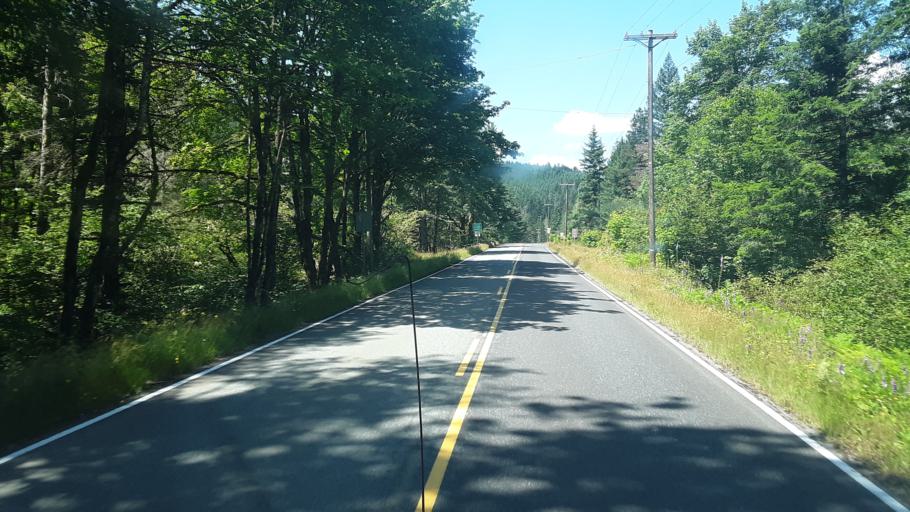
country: US
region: Washington
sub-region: Clark County
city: Amboy
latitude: 46.0559
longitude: -122.2436
